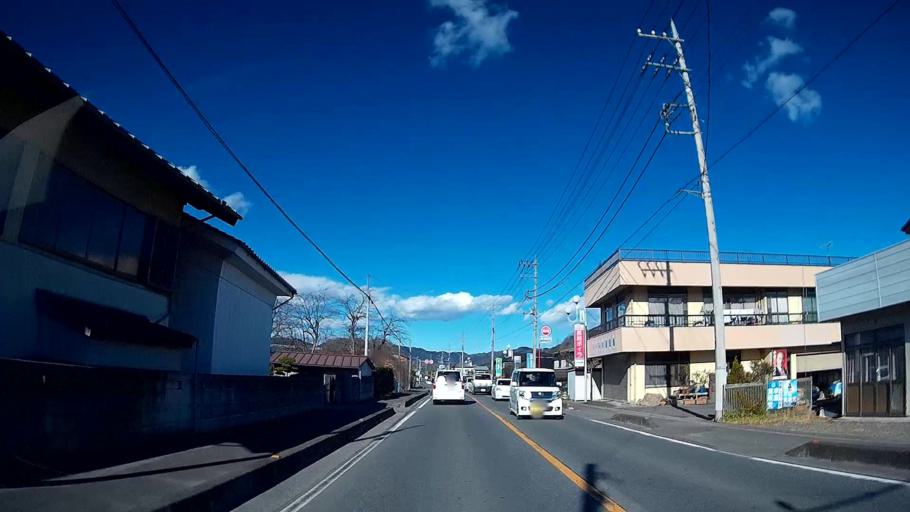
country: JP
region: Saitama
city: Yorii
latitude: 36.0863
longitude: 139.1129
